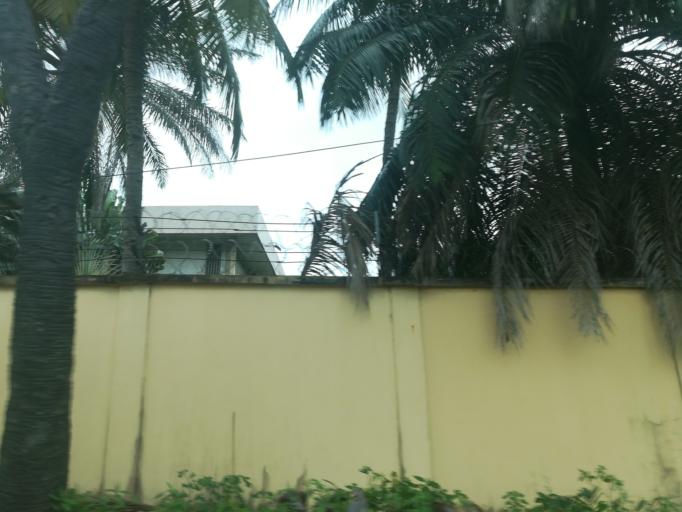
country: NG
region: Lagos
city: Lagos
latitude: 6.4394
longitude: 3.4091
